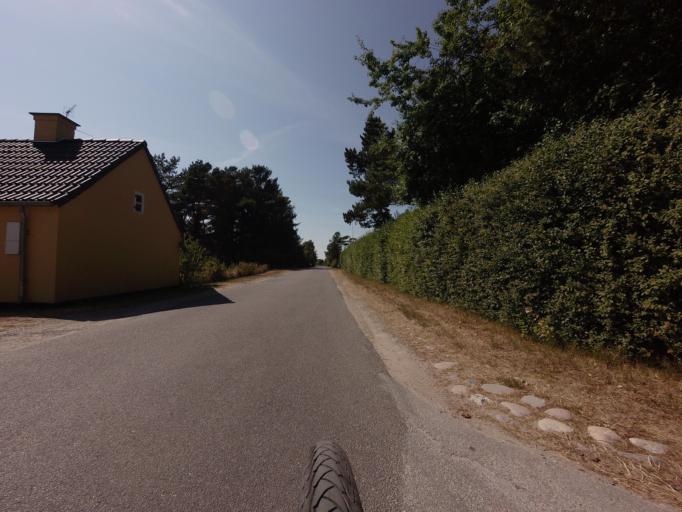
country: DK
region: North Denmark
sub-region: Laeso Kommune
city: Byrum
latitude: 57.2950
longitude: 10.9340
